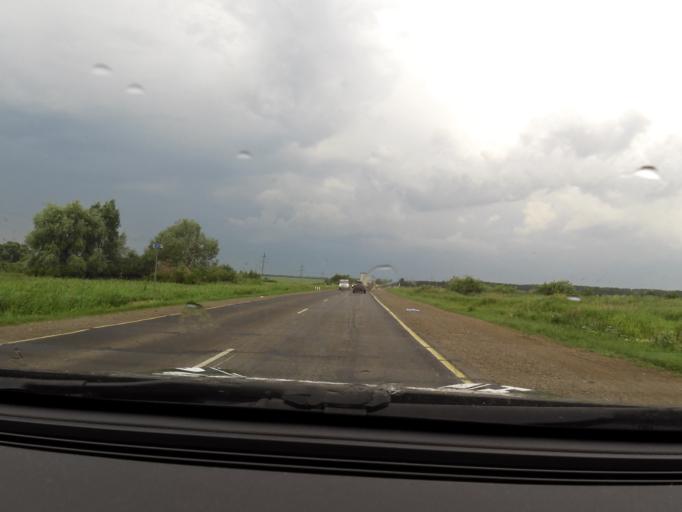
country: RU
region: Bashkortostan
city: Asanovo
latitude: 54.9111
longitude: 55.5971
